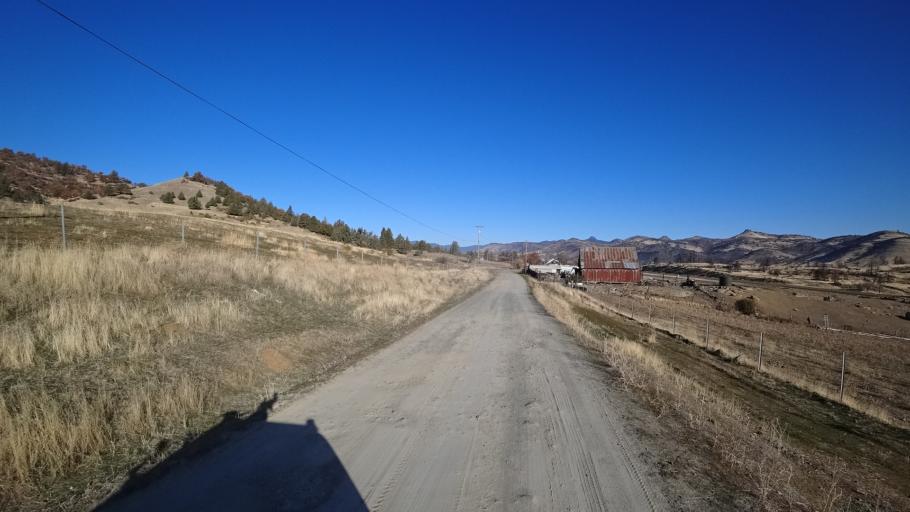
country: US
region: California
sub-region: Siskiyou County
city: Montague
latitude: 41.8920
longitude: -122.5640
